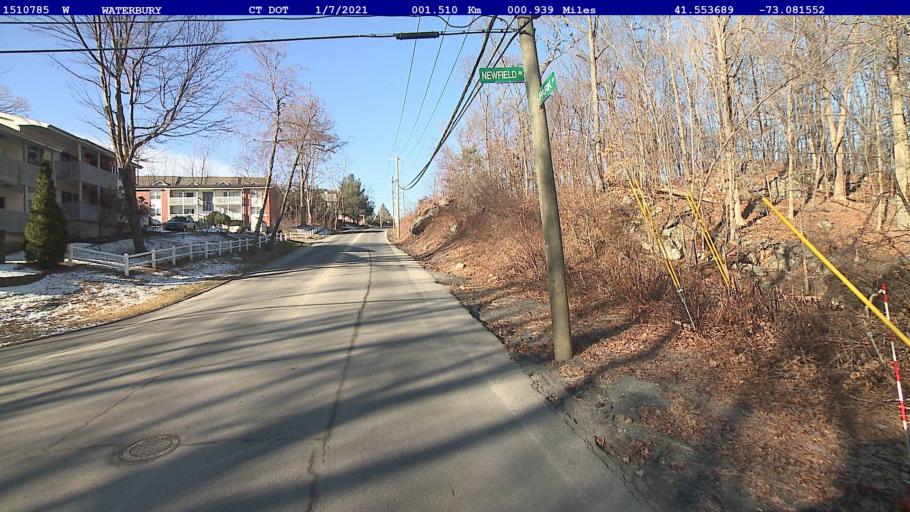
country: US
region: Connecticut
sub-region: New Haven County
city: Waterbury
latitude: 41.5537
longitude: -73.0816
